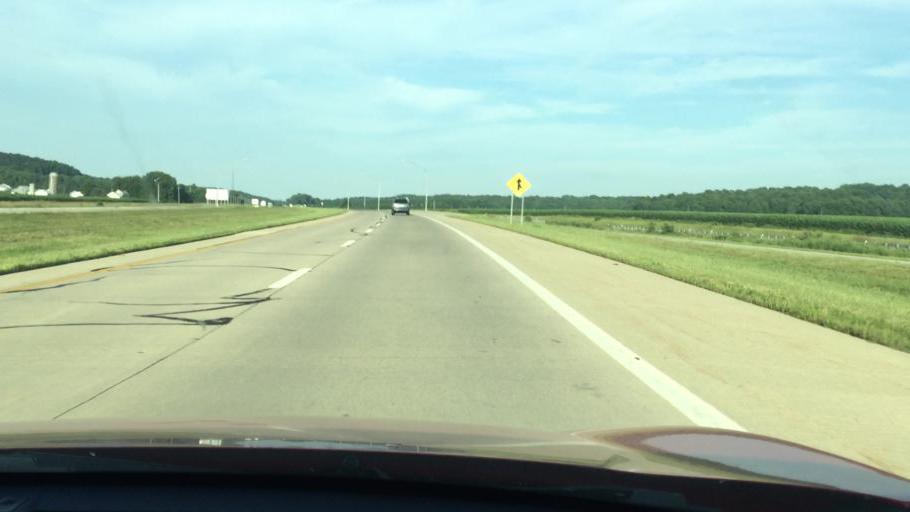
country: US
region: Ohio
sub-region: Logan County
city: Bellefontaine
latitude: 40.3245
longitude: -83.6599
